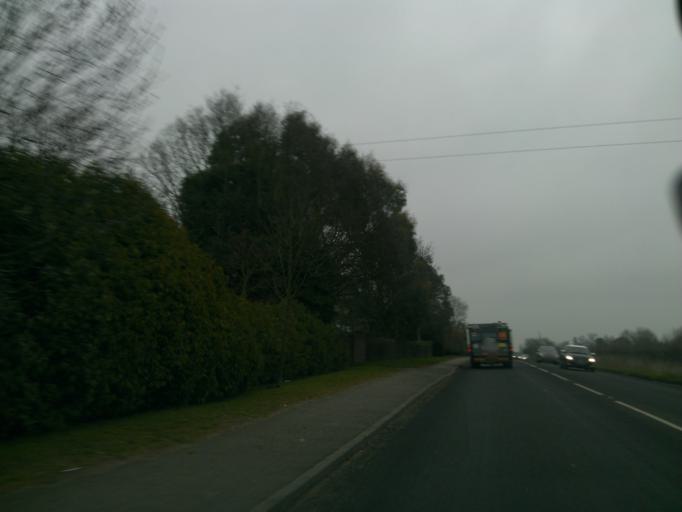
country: GB
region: England
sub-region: Essex
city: Alresford
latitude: 51.8690
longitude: 1.0182
